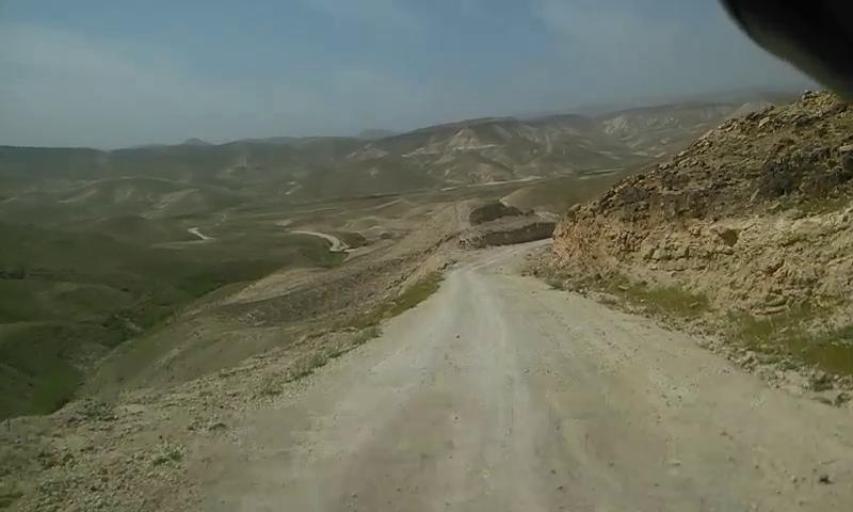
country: PS
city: `Arab ar Rashaydah
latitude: 31.5152
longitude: 35.2872
